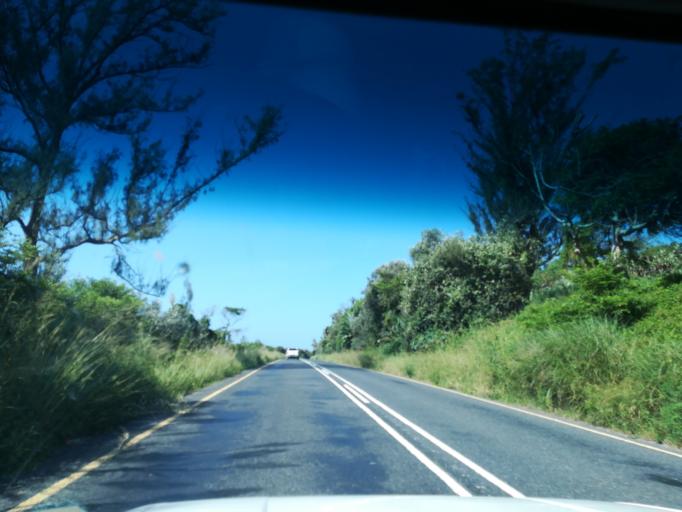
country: ZA
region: KwaZulu-Natal
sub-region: Ugu District Municipality
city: Scottburgh
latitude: -30.3377
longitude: 30.7318
